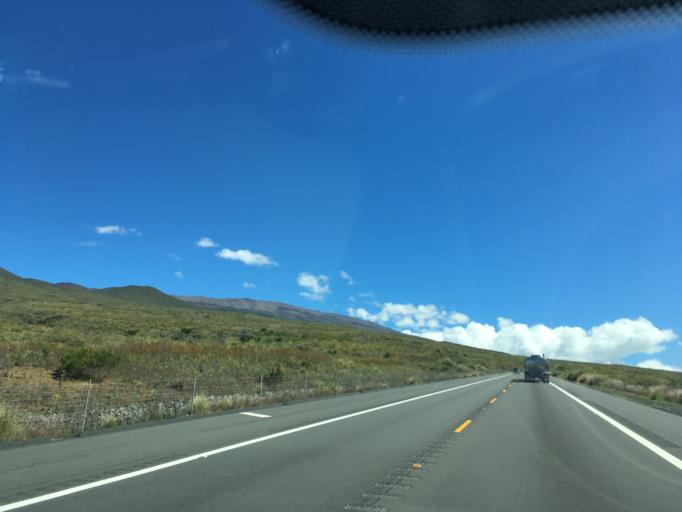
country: US
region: Hawaii
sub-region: Hawaii County
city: Waikoloa
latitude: 19.7791
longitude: -155.6018
